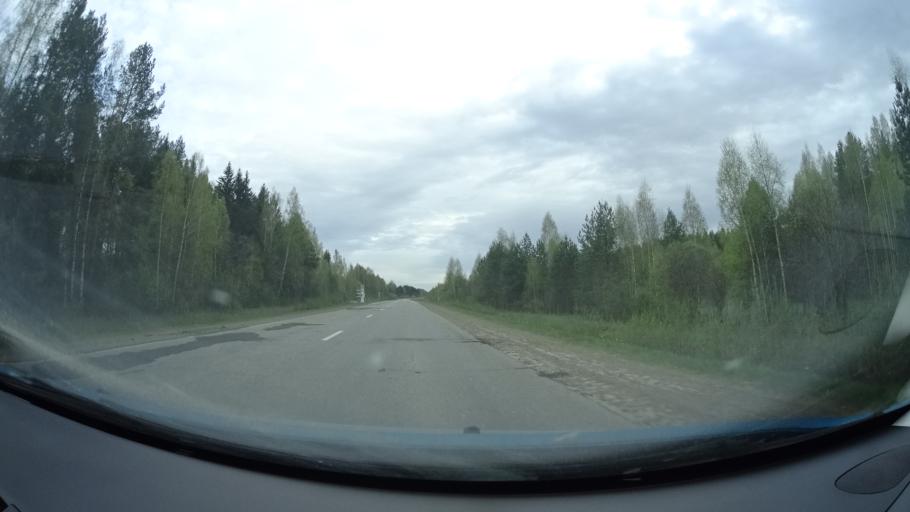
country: RU
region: Perm
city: Osa
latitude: 57.3588
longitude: 55.6007
